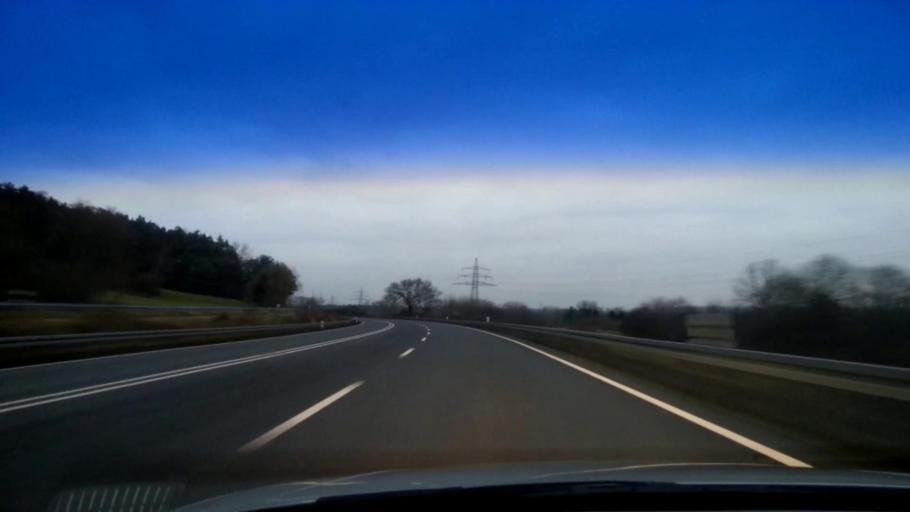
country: DE
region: Bavaria
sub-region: Upper Franconia
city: Hirschaid
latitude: 49.8116
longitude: 10.9643
